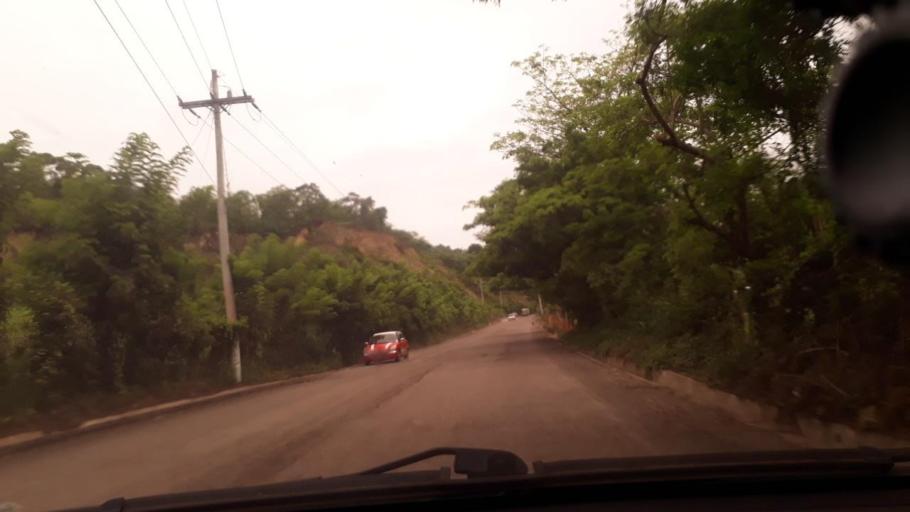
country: GT
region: Chiquimula
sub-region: Municipio de San Juan Ermita
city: San Juan Ermita
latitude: 14.7542
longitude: -89.4447
